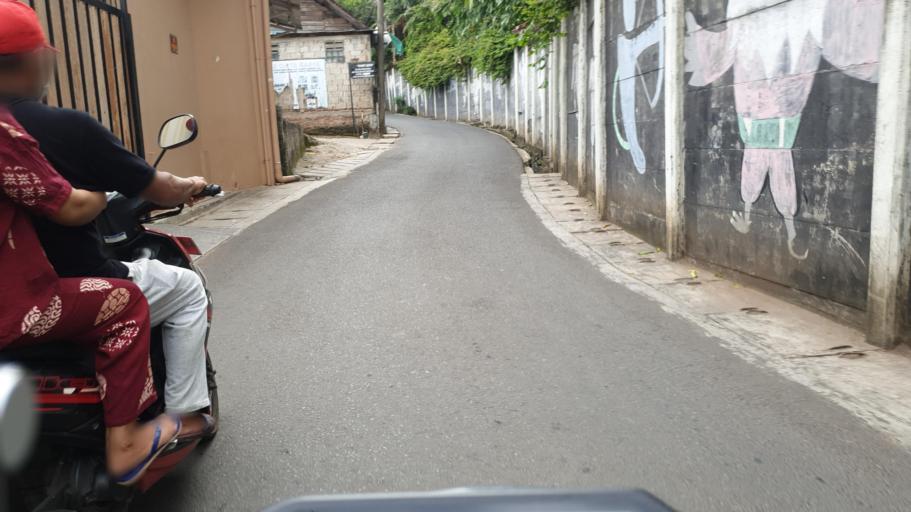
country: ID
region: Banten
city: South Tangerang
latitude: -6.2753
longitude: 106.7915
